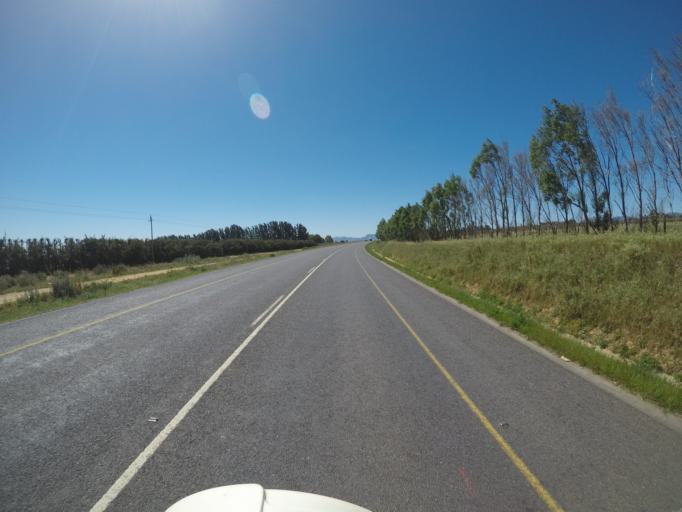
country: ZA
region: Western Cape
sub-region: Cape Winelands District Municipality
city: Noorder-Paarl
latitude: -33.6788
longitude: 18.9026
